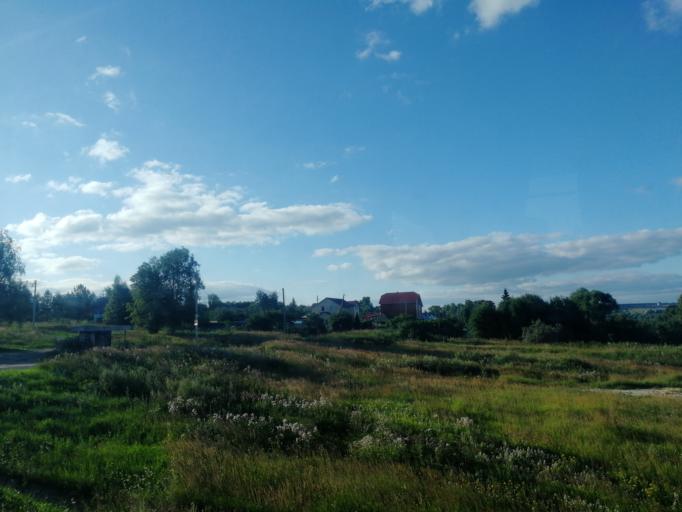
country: RU
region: Tula
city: Novogurovskiy
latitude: 54.2812
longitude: 37.1748
